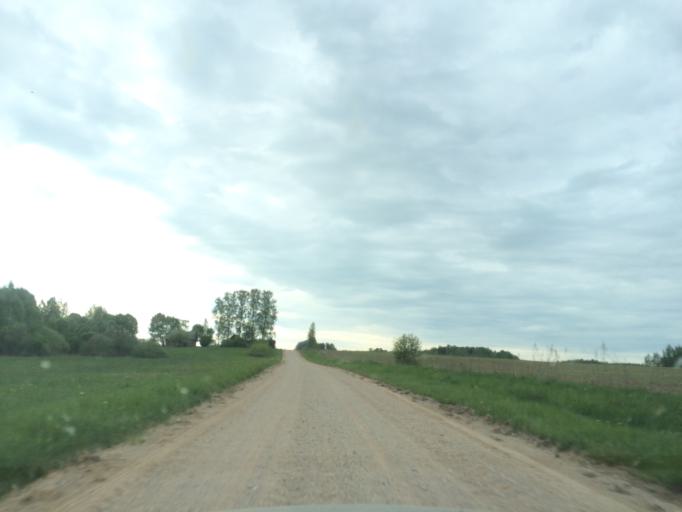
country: LV
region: Ludzas Rajons
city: Ludza
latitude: 56.5920
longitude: 27.5296
